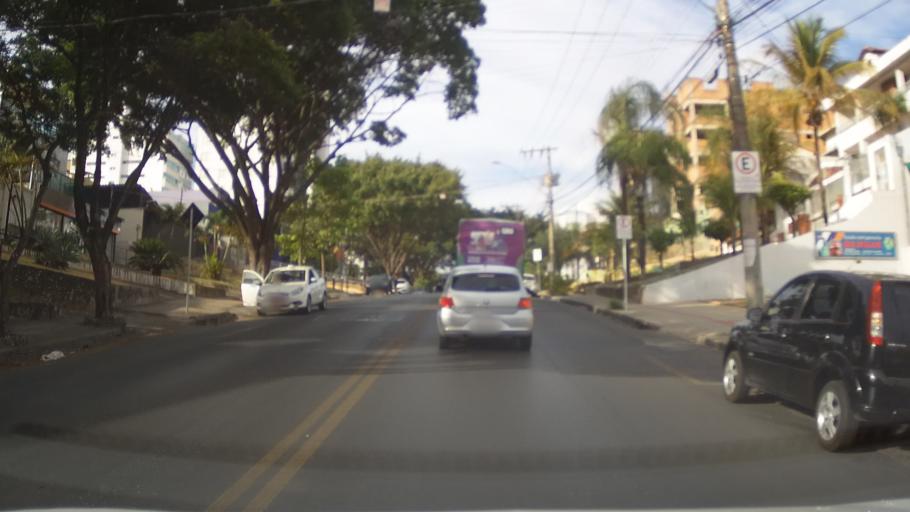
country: BR
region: Minas Gerais
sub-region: Belo Horizonte
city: Belo Horizonte
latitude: -19.8797
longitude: -43.9976
